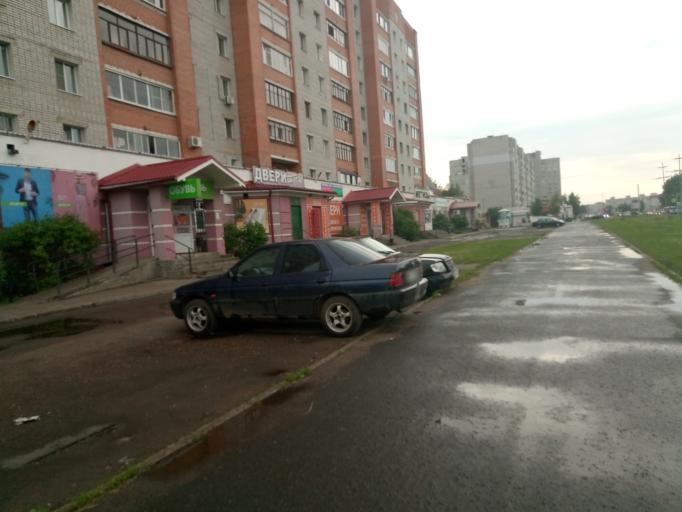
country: RU
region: Jaroslavl
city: Yaroslavl
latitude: 57.6414
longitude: 39.9596
